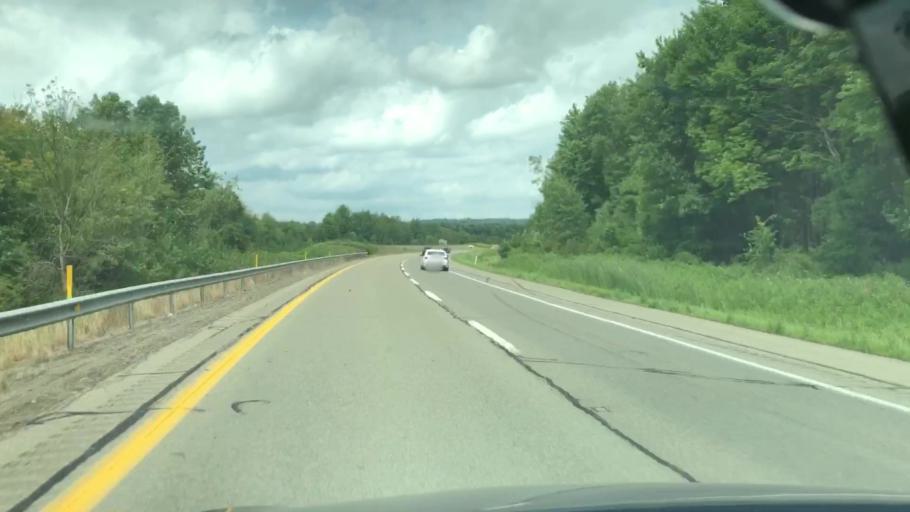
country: US
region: Pennsylvania
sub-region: Crawford County
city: Meadville
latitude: 41.7267
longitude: -80.2051
